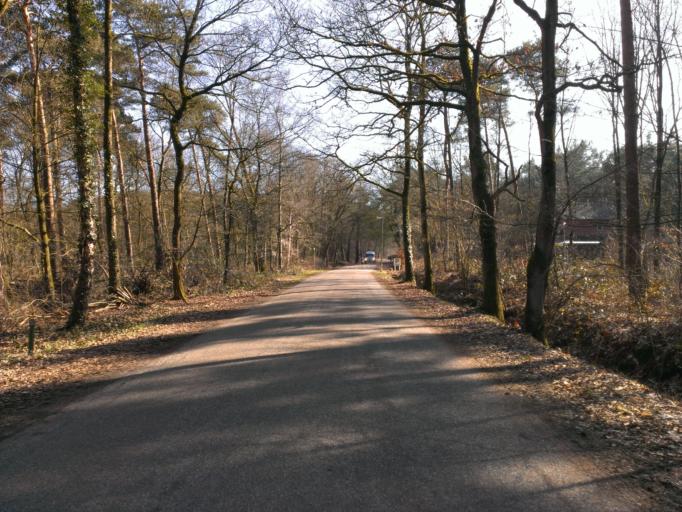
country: NL
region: Overijssel
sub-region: Gemeente Almelo
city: Almelo
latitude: 52.3301
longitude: 6.6830
